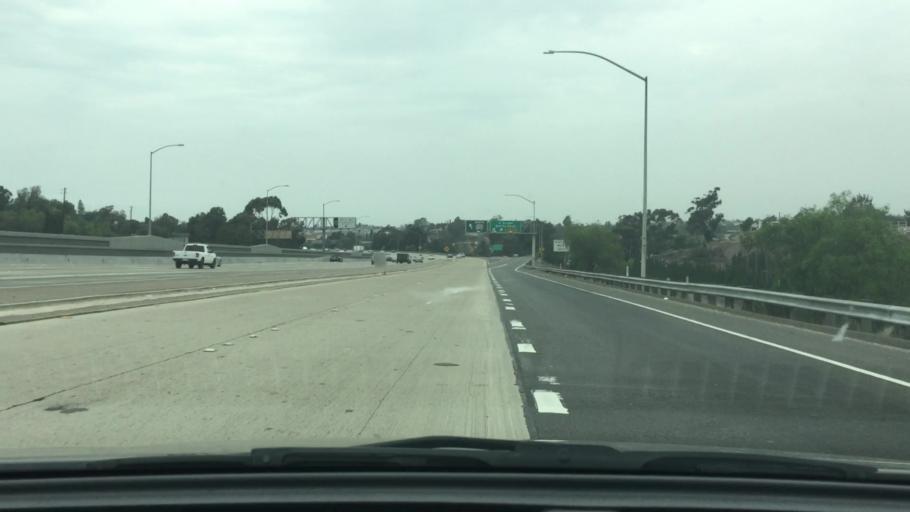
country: US
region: California
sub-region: San Diego County
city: Chula Vista
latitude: 32.6431
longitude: -117.0568
